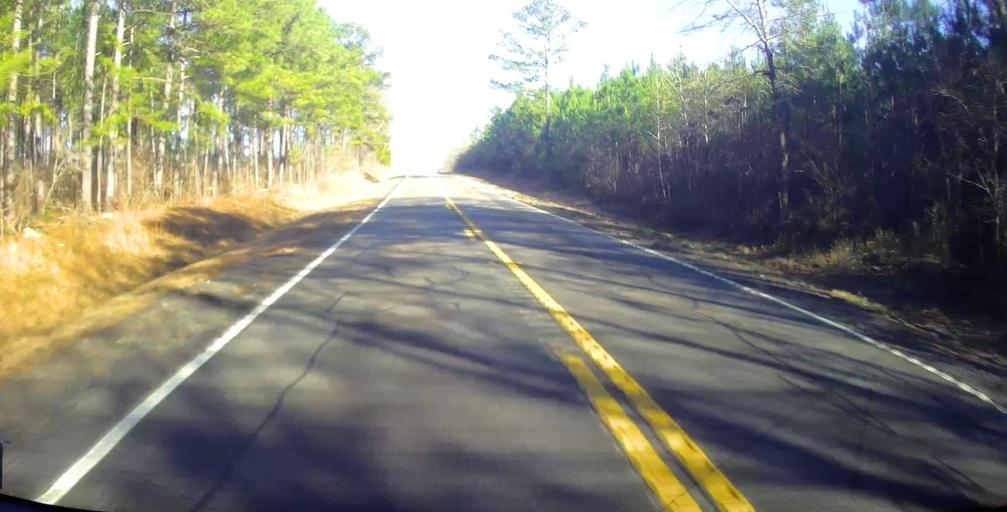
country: US
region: Georgia
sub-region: Talbot County
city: Talbotton
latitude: 32.6725
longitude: -84.5022
